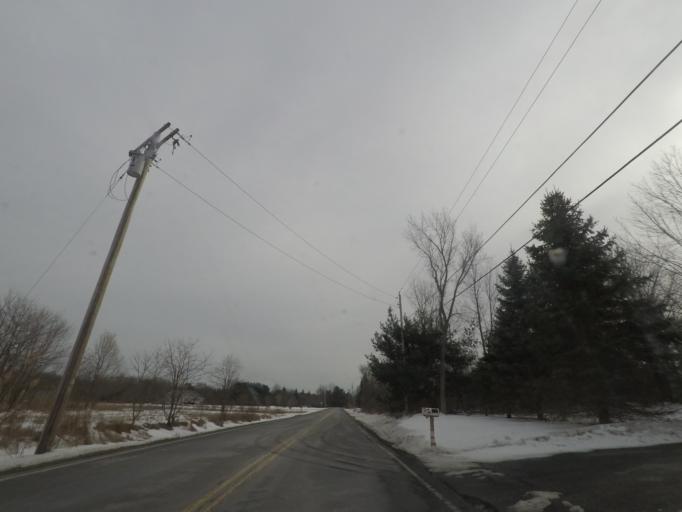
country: US
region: New York
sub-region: Albany County
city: Altamont
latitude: 42.6867
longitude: -73.9837
